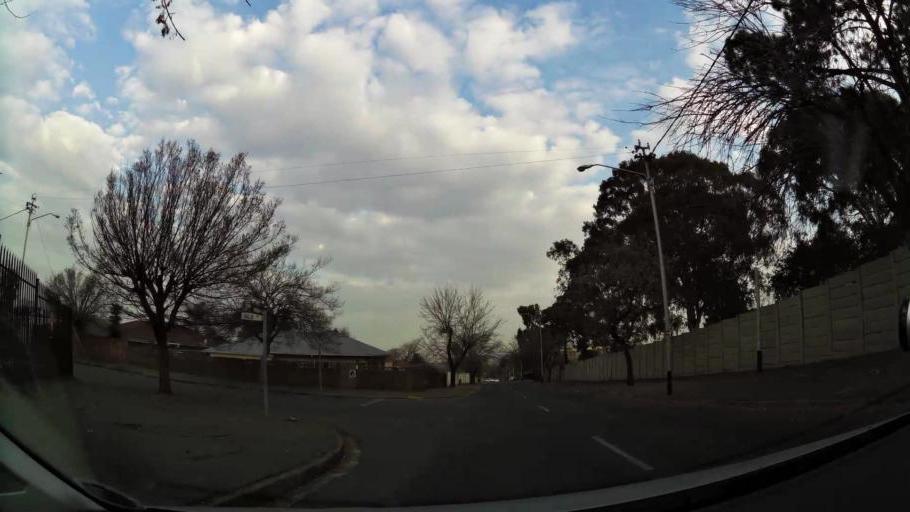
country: ZA
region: Gauteng
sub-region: Ekurhuleni Metropolitan Municipality
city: Germiston
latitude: -26.1771
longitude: 28.1704
